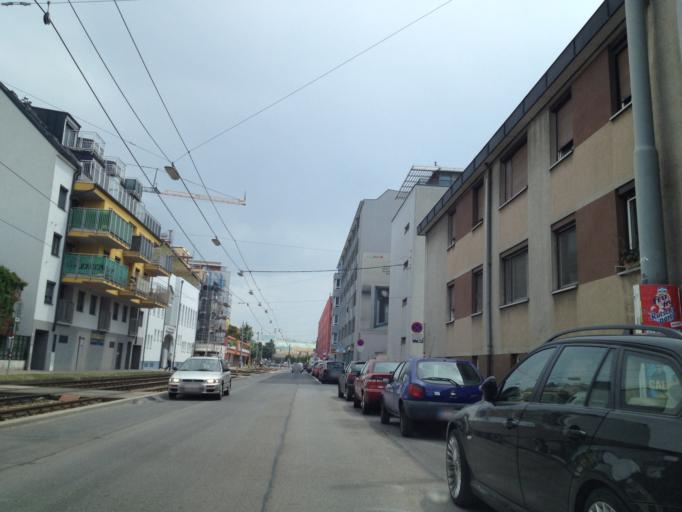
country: AT
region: Lower Austria
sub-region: Politischer Bezirk Wien-Umgebung
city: Gerasdorf bei Wien
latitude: 48.2234
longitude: 16.4563
